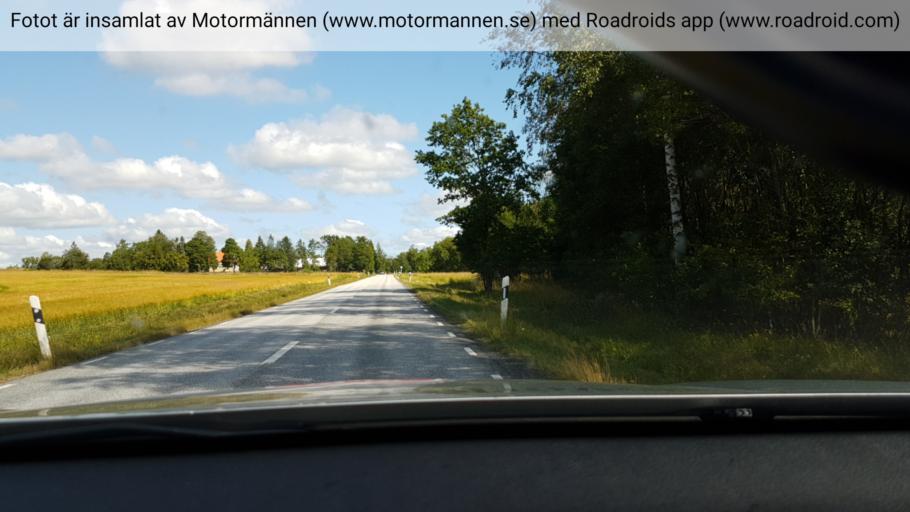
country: SE
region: Stockholm
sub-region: Norrtalje Kommun
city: Hallstavik
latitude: 59.9291
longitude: 18.7102
